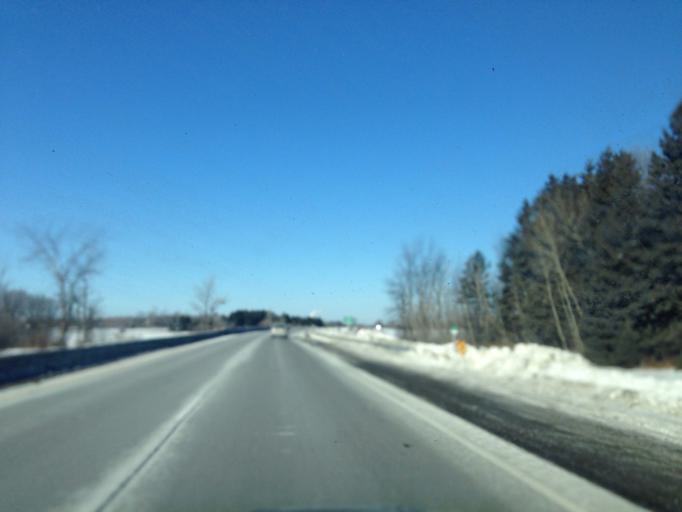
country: CA
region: Ontario
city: Ottawa
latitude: 45.3737
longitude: -75.5638
